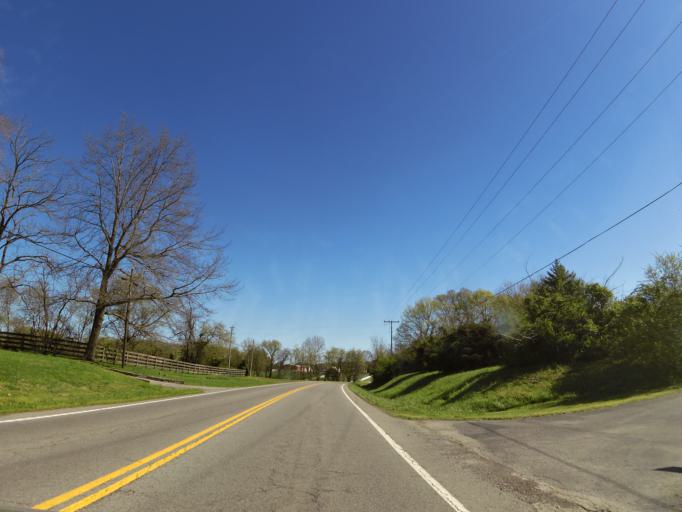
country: US
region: Tennessee
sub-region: Robertson County
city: Springfield
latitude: 36.5390
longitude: -86.8788
